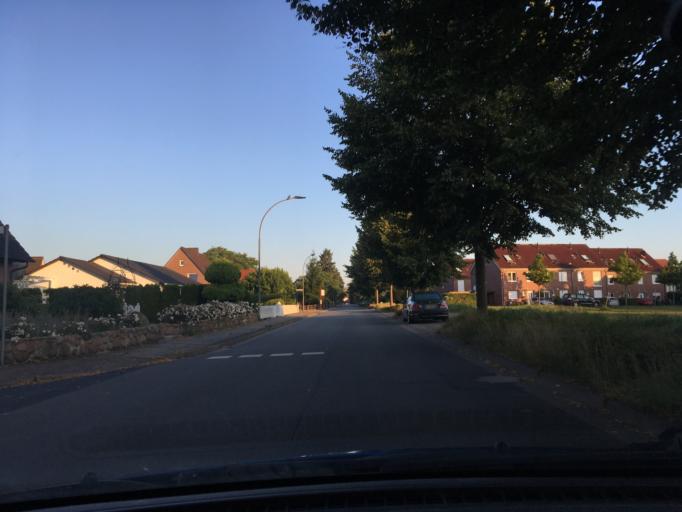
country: DE
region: Lower Saxony
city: Seevetal
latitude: 53.3846
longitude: 9.9910
